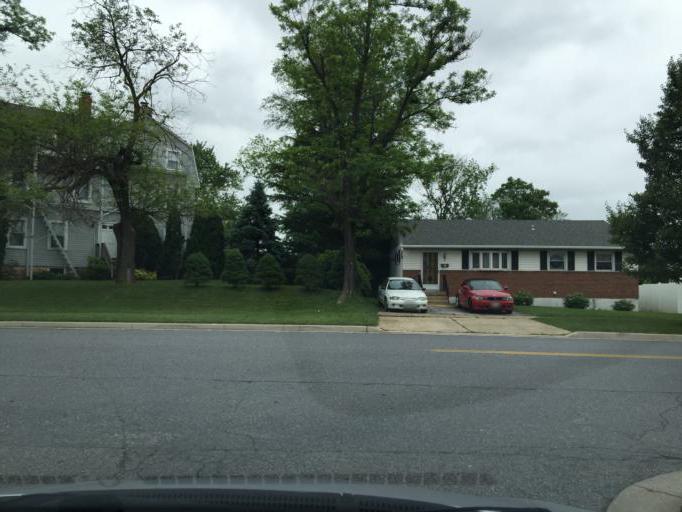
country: US
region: Maryland
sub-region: Baltimore County
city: Timonium
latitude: 39.4429
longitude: -76.6235
